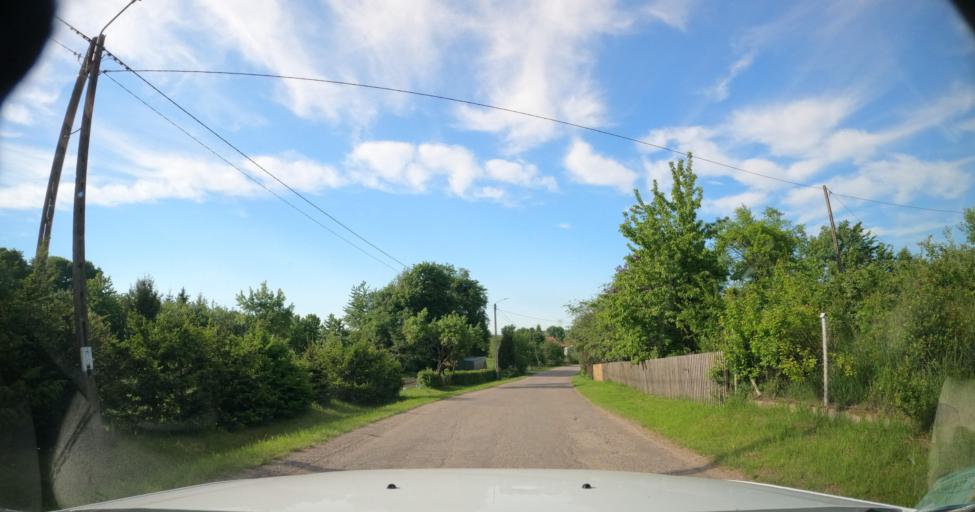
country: PL
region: Warmian-Masurian Voivodeship
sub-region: Powiat ostrodzki
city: Morag
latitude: 54.0657
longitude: 19.8890
